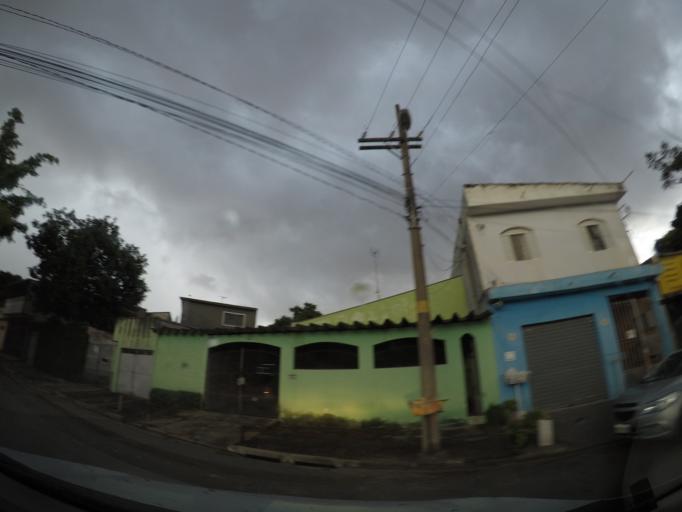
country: BR
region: Sao Paulo
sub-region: Guarulhos
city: Guarulhos
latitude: -23.4685
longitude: -46.5627
